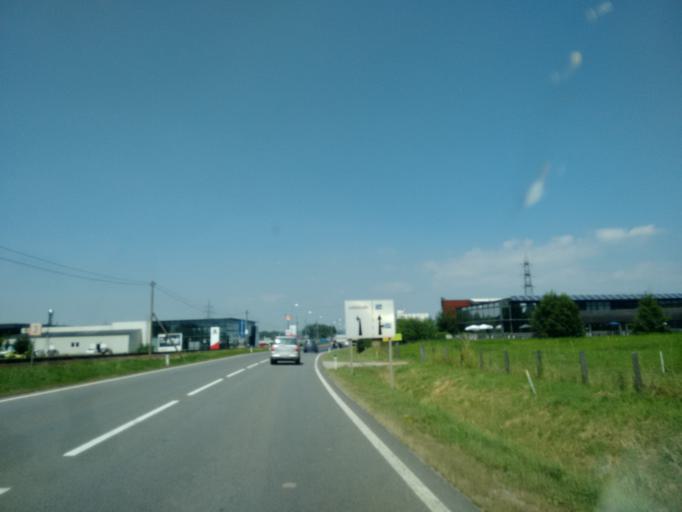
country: AT
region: Upper Austria
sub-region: Politischer Bezirk Urfahr-Umgebung
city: Feldkirchen an der Donau
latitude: 48.2958
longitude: 14.0106
